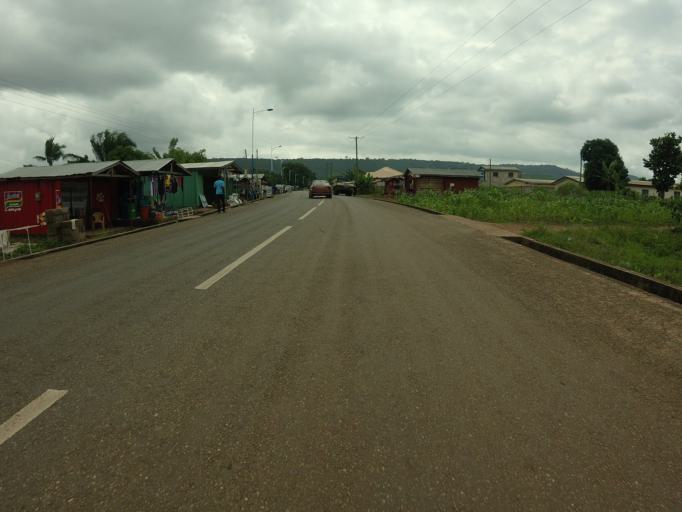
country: GH
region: Volta
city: Ho
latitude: 6.6291
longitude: 0.4883
